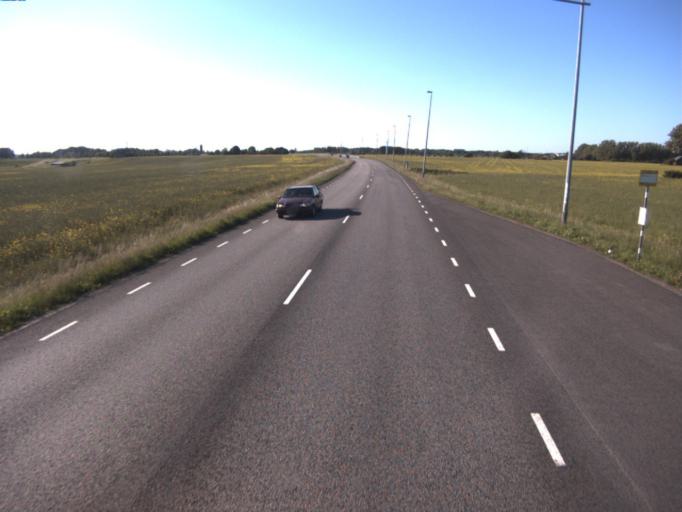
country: SE
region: Skane
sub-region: Helsingborg
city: Rydeback
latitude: 55.9823
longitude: 12.7700
